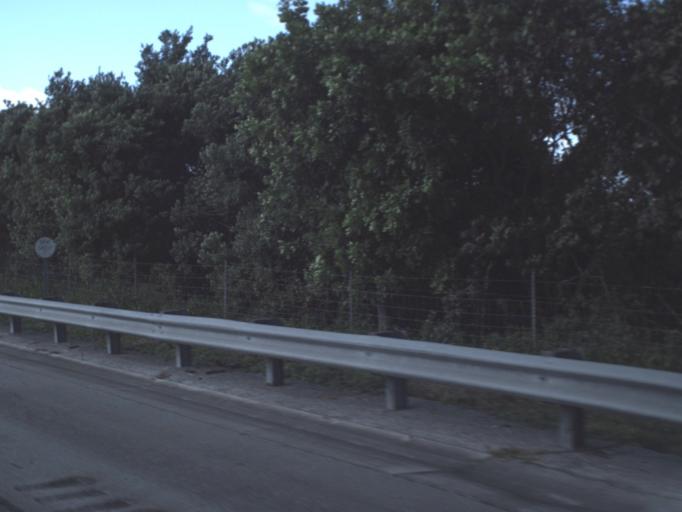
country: US
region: Florida
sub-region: Broward County
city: Coral Springs
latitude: 26.2853
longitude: -80.2973
